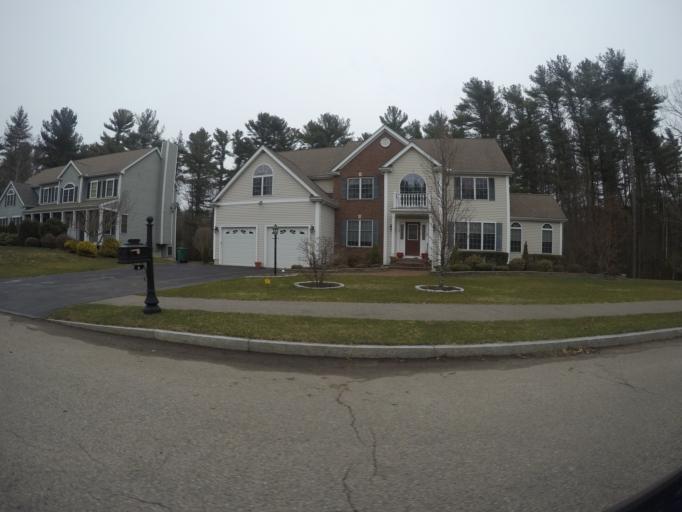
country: US
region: Massachusetts
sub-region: Bristol County
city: Easton
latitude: 42.0192
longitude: -71.1101
